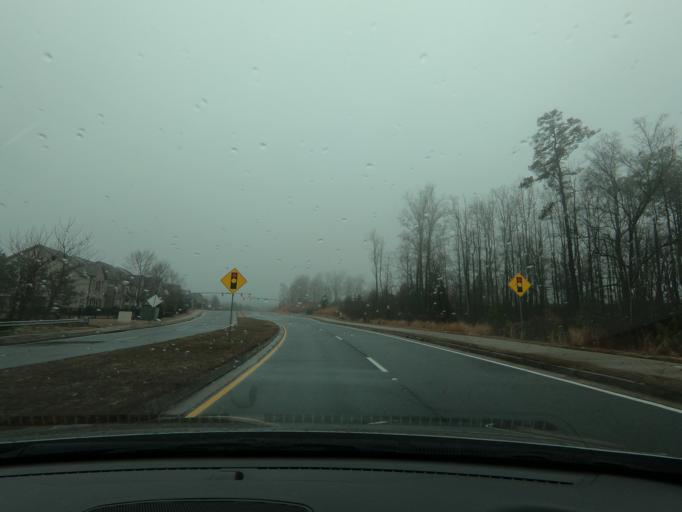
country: US
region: Georgia
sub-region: Fulton County
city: Alpharetta
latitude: 34.1054
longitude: -84.2317
